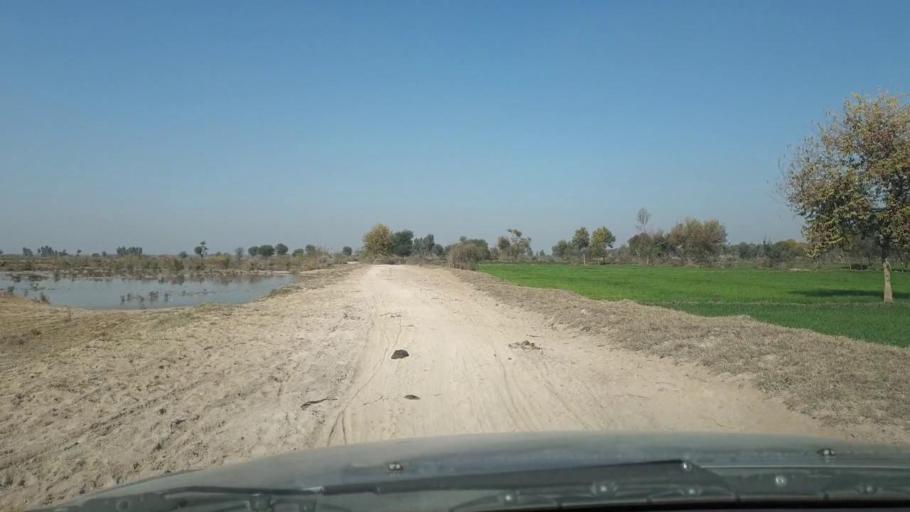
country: PK
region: Sindh
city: Adilpur
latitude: 27.8893
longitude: 69.2561
